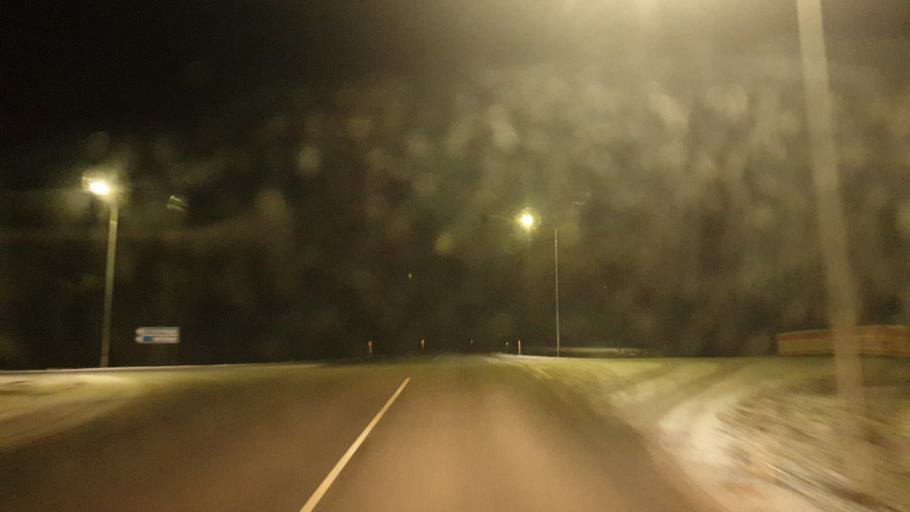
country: FI
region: Southern Savonia
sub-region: Pieksaemaeki
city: Juva
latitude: 61.8759
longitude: 27.7706
